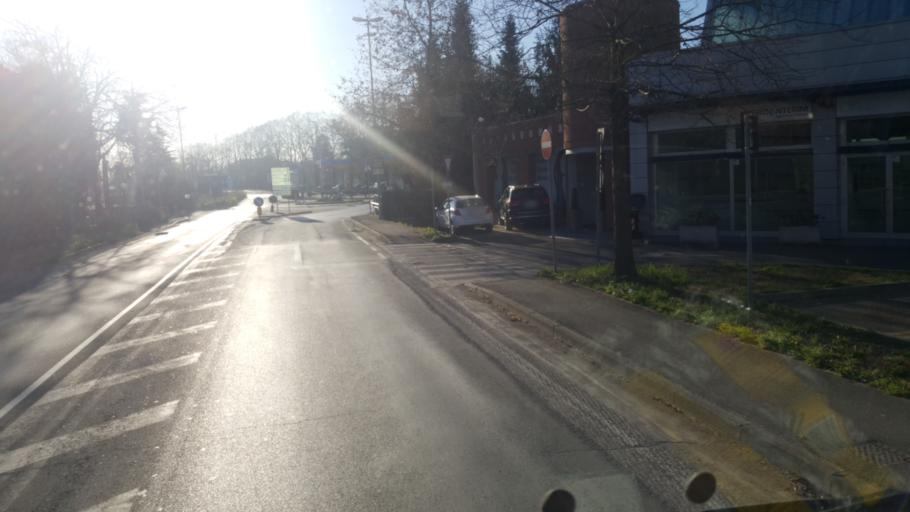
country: IT
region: Emilia-Romagna
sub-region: Provincia di Reggio Emilia
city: Rubiera
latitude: 44.6533
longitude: 10.7867
